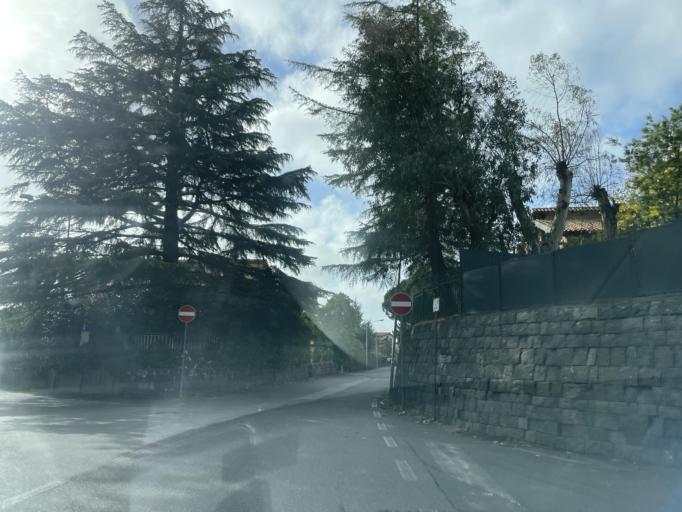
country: IT
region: Sicily
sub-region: Catania
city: Nicolosi
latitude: 37.6201
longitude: 15.0242
